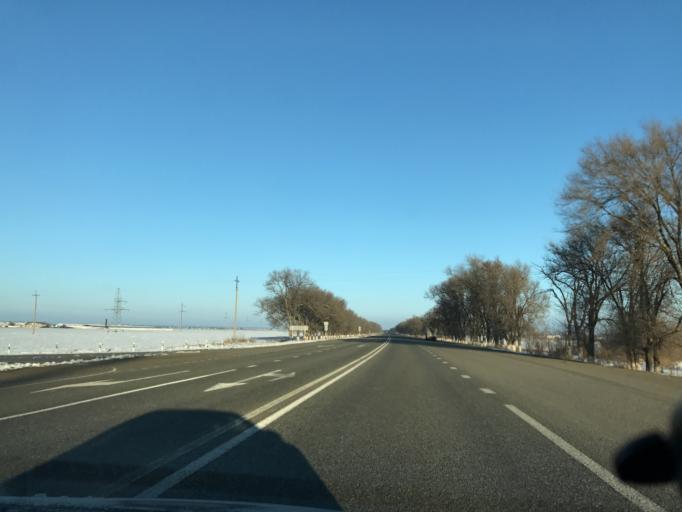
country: RU
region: Stavropol'skiy
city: Bezopasnoye
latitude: 45.6178
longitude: 41.9398
